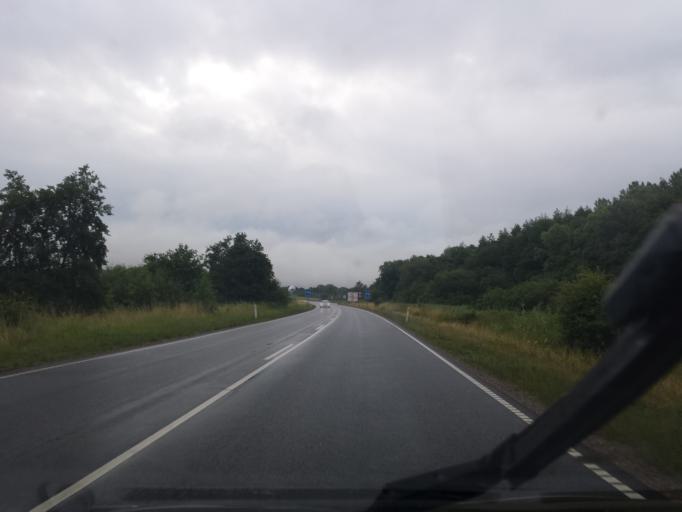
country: DK
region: South Denmark
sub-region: Sonderborg Kommune
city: Sonderborg
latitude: 54.9304
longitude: 9.8369
